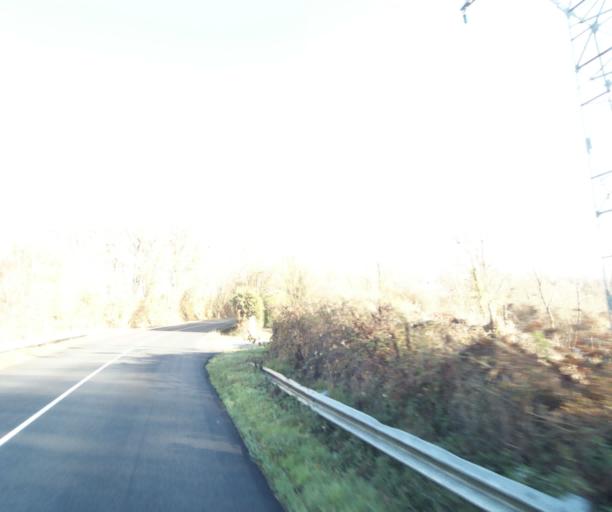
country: FR
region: Poitou-Charentes
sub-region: Departement de la Charente-Maritime
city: Fontcouverte
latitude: 45.7592
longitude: -0.5571
